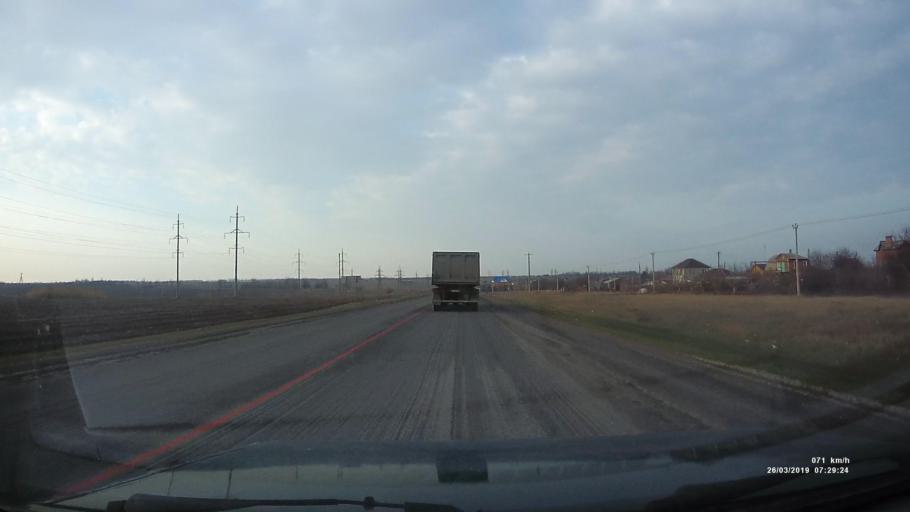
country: RU
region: Rostov
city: Novobessergenovka
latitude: 47.2455
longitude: 38.8168
